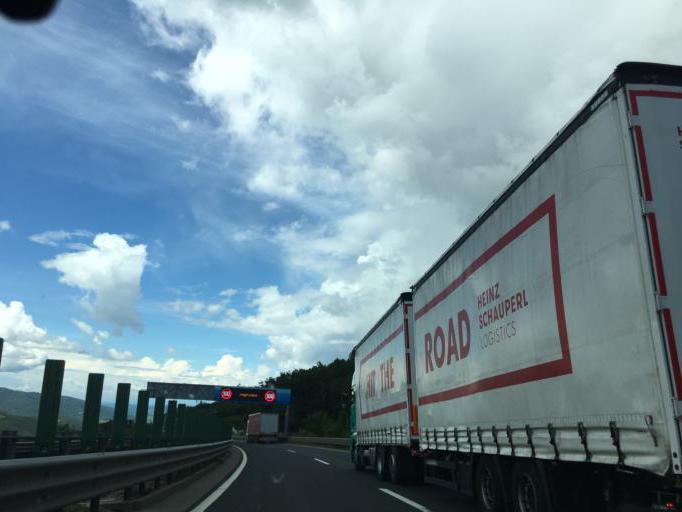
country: SI
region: Divaca
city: Divaca
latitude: 45.7613
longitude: 14.0431
